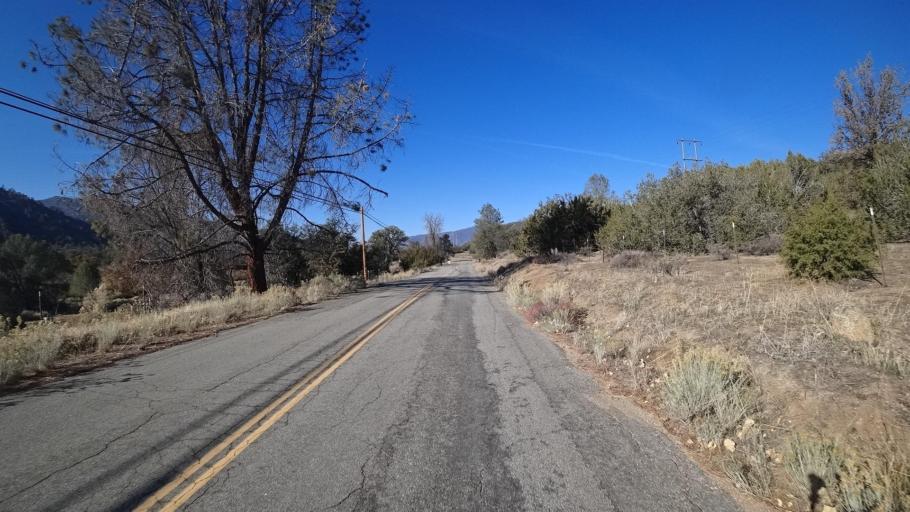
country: US
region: California
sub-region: Kern County
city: Bodfish
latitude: 35.3980
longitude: -118.4551
